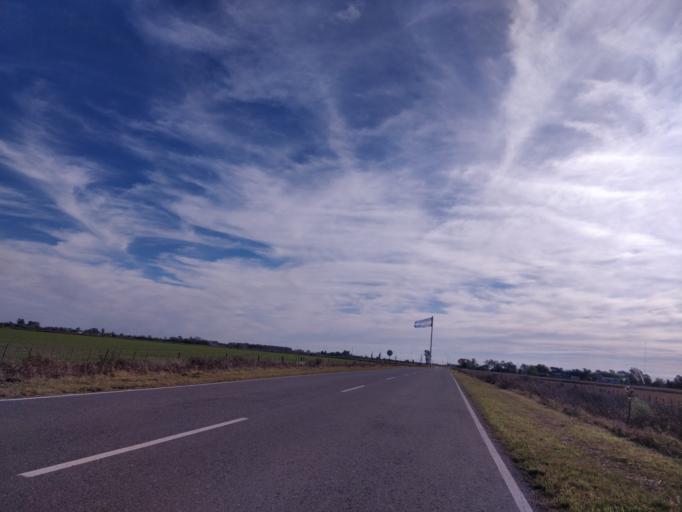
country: AR
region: Cordoba
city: Leones
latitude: -32.6430
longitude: -62.2855
